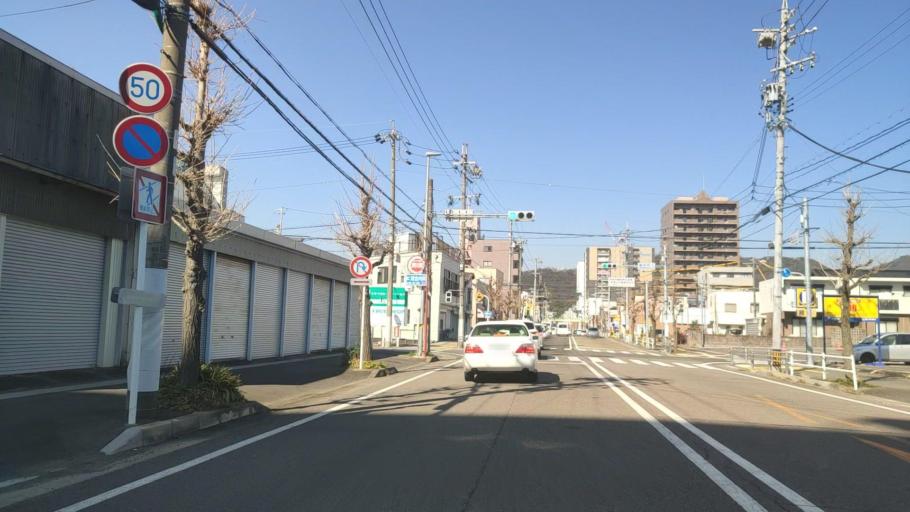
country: JP
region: Gifu
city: Gifu-shi
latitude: 35.4100
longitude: 136.7673
